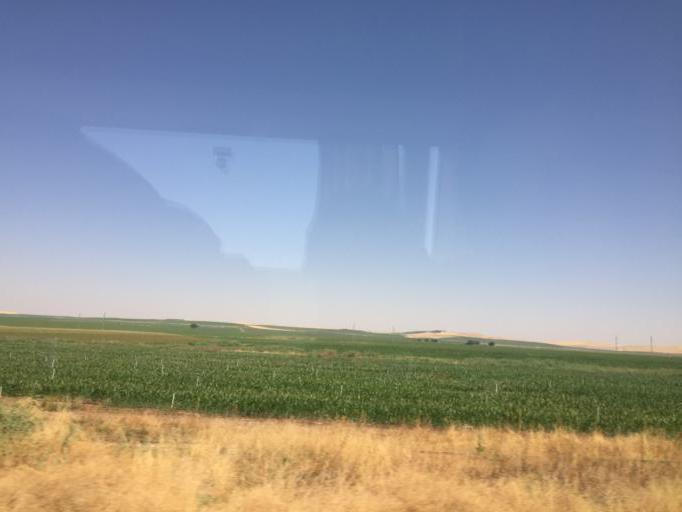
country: TR
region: Diyarbakir
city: Tepe
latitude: 37.8507
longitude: 40.7680
